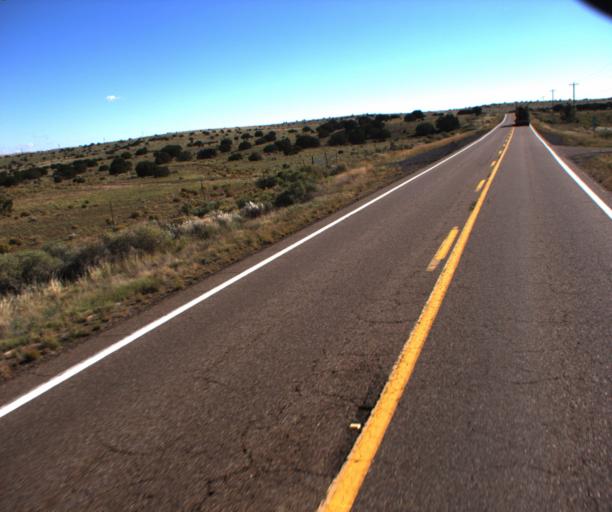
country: US
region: Arizona
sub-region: Apache County
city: Saint Johns
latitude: 34.4854
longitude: -109.5437
